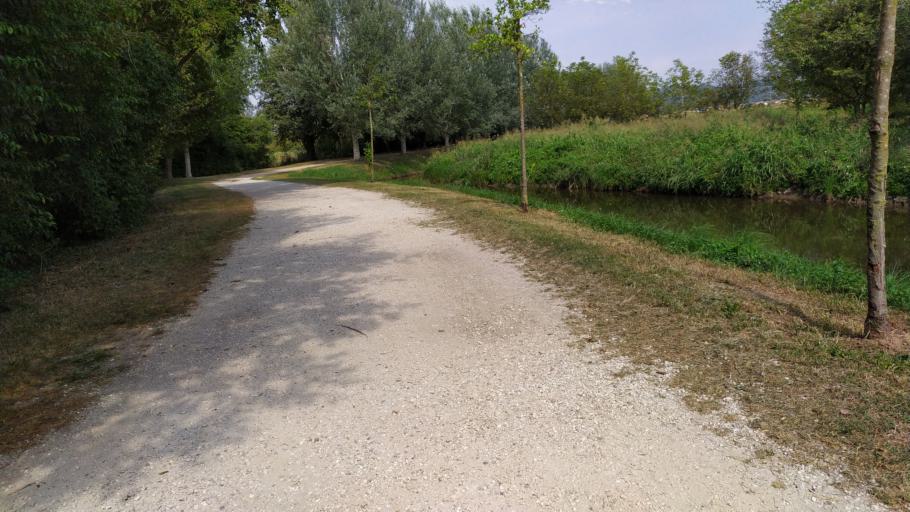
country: IT
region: Veneto
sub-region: Provincia di Vicenza
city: Arcugnano-Torri
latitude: 45.4765
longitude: 11.5461
